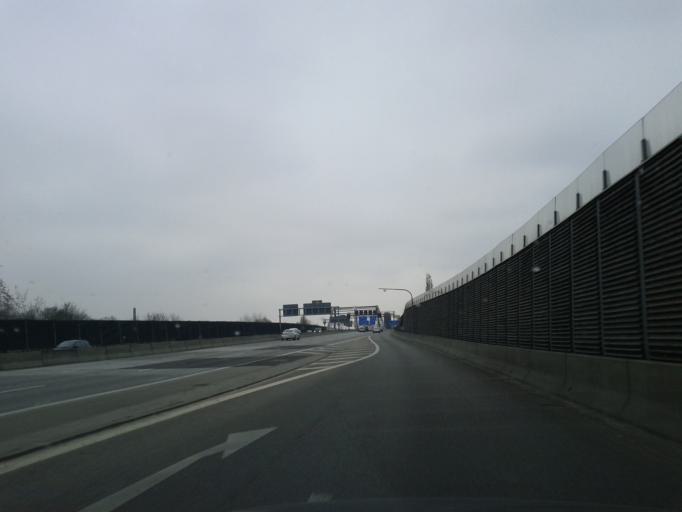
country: DE
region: Berlin
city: Buckow
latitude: 52.4557
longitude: 13.4606
